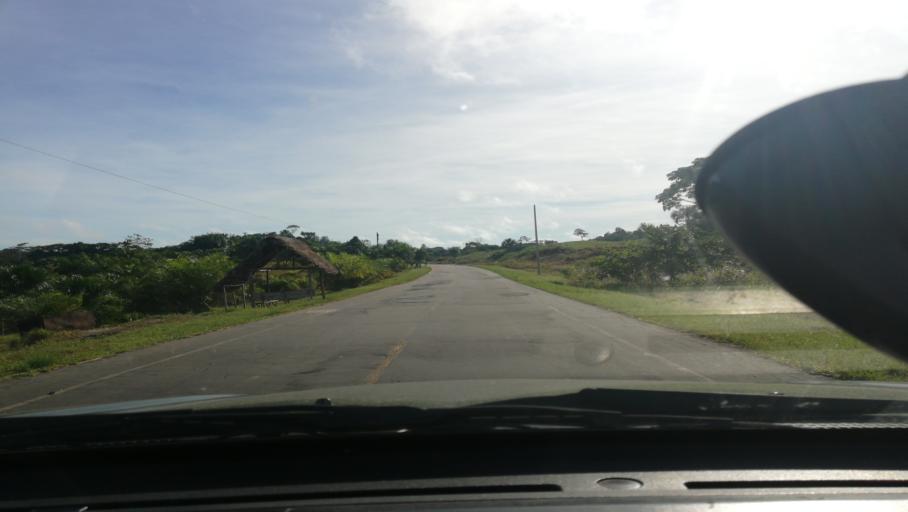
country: PE
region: Loreto
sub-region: Provincia de Loreto
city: Nauta
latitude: -4.3452
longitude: -73.5412
